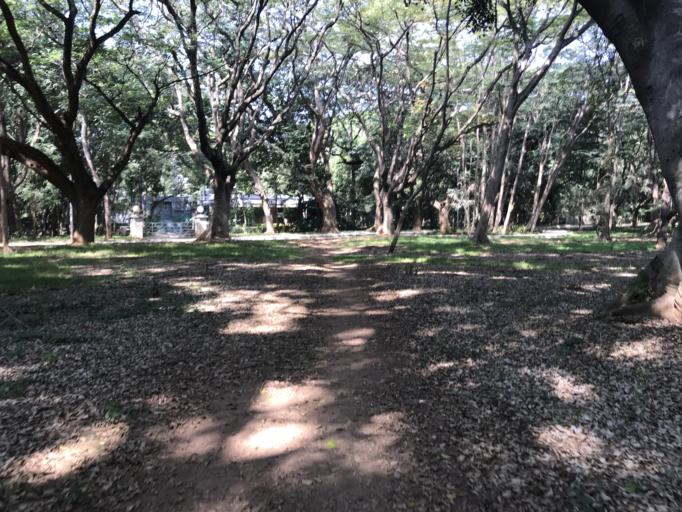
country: IN
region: Karnataka
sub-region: Bangalore Urban
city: Bangalore
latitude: 13.0194
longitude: 77.5667
